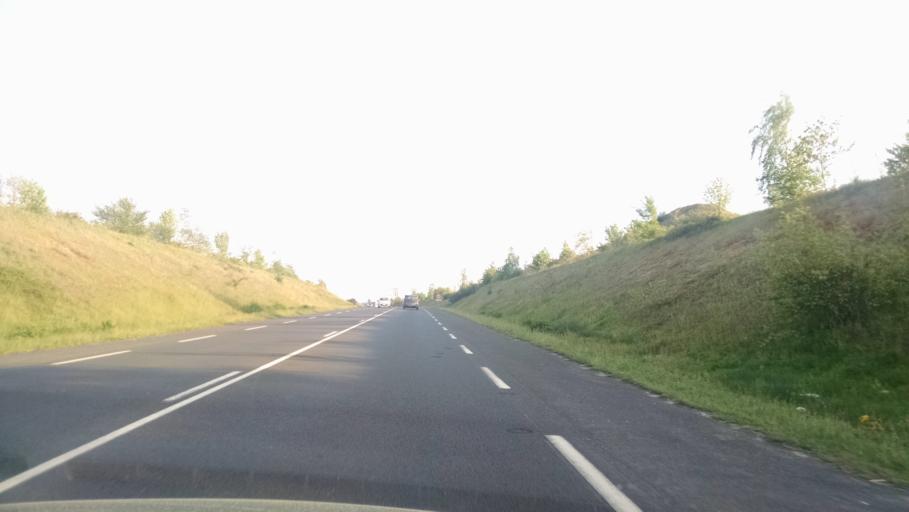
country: FR
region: Pays de la Loire
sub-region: Departement de la Loire-Atlantique
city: Getigne
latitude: 47.0890
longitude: -1.2631
